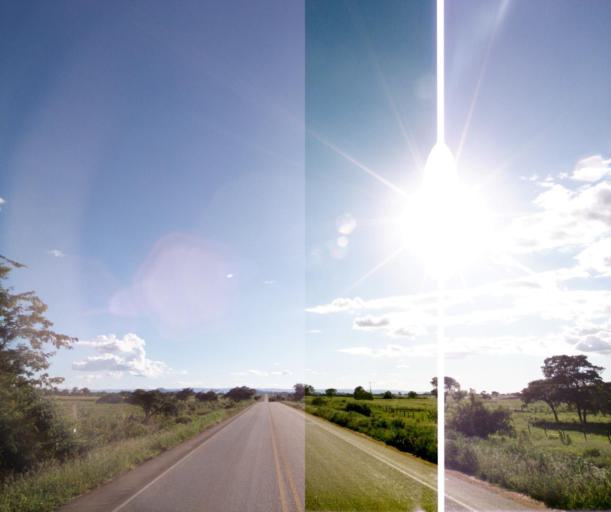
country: BR
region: Bahia
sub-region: Guanambi
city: Guanambi
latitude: -14.1923
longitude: -42.7454
